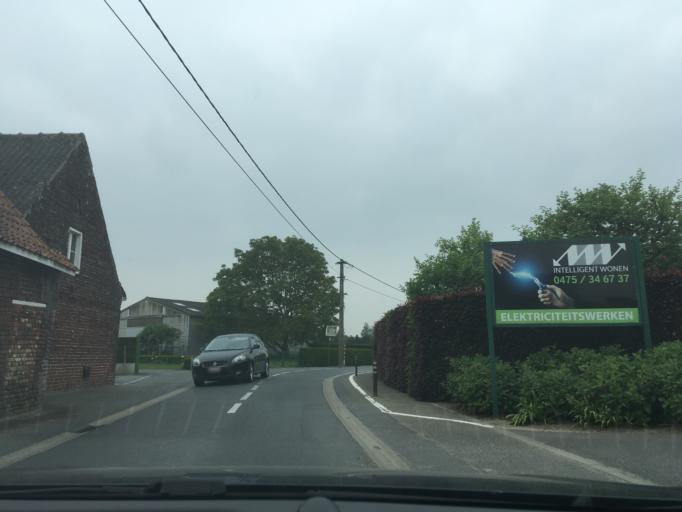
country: BE
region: Flanders
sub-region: Provincie West-Vlaanderen
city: Lichtervelde
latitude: 51.0195
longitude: 3.1405
